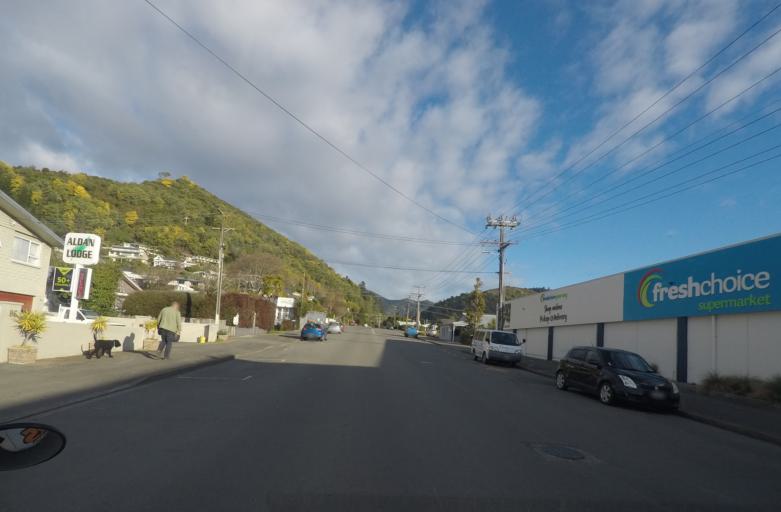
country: NZ
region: Marlborough
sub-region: Marlborough District
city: Picton
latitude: -41.2920
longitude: 174.0078
